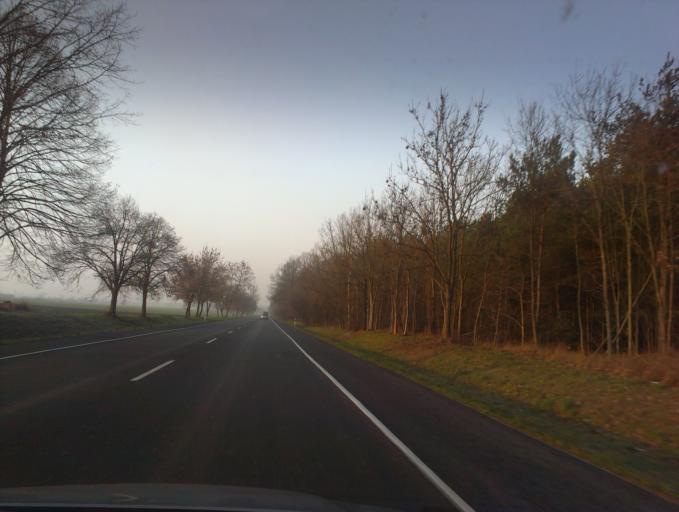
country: PL
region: Greater Poland Voivodeship
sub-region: Powiat obornicki
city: Oborniki
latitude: 52.6891
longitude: 16.8843
